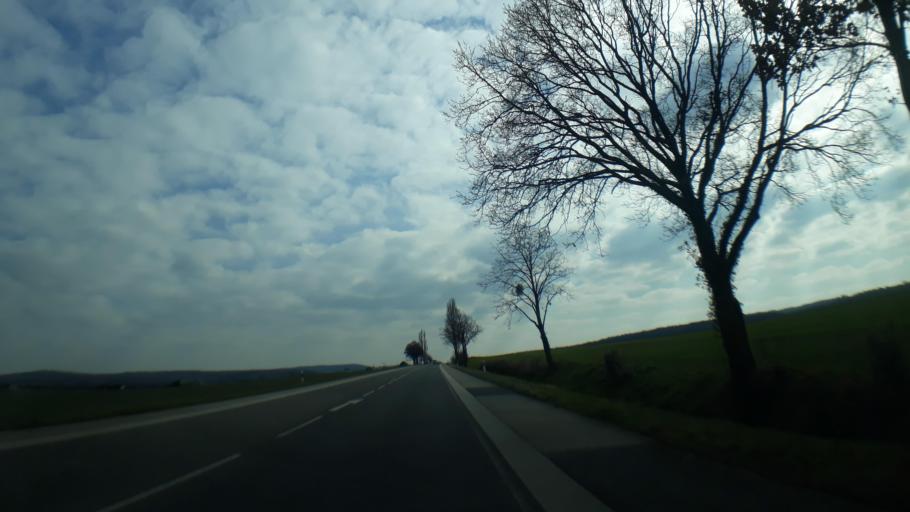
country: DE
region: North Rhine-Westphalia
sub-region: Regierungsbezirk Koln
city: Euskirchen
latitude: 50.6105
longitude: 6.8521
